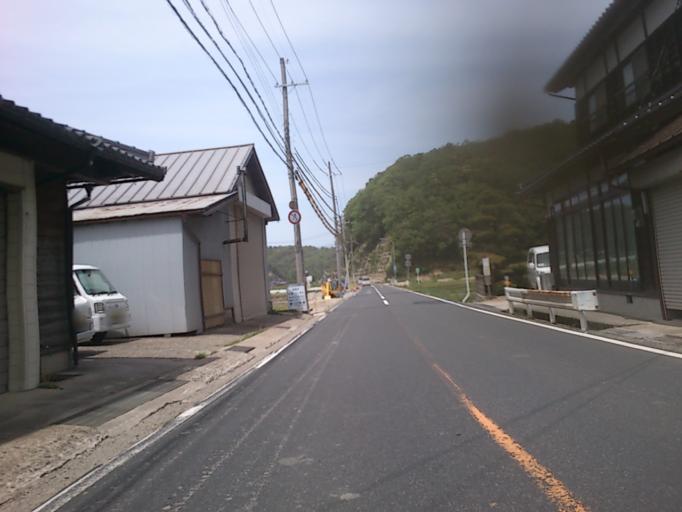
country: JP
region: Kyoto
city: Miyazu
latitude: 35.6879
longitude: 135.0980
